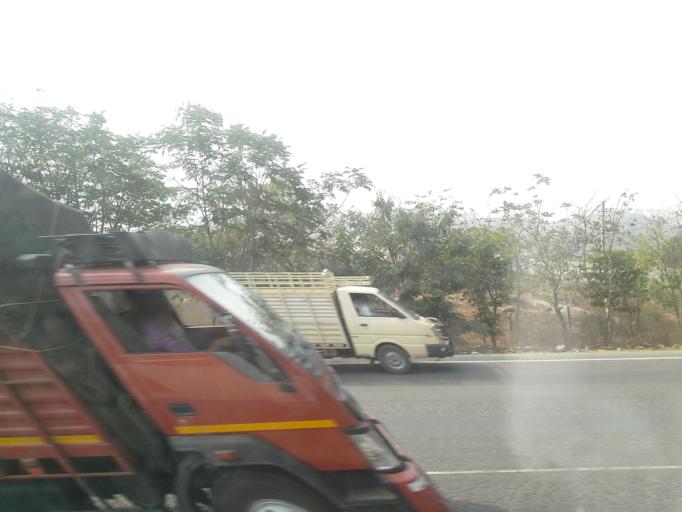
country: IN
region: Telangana
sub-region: Rangareddi
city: Lal Bahadur Nagar
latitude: 17.3135
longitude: 78.6779
